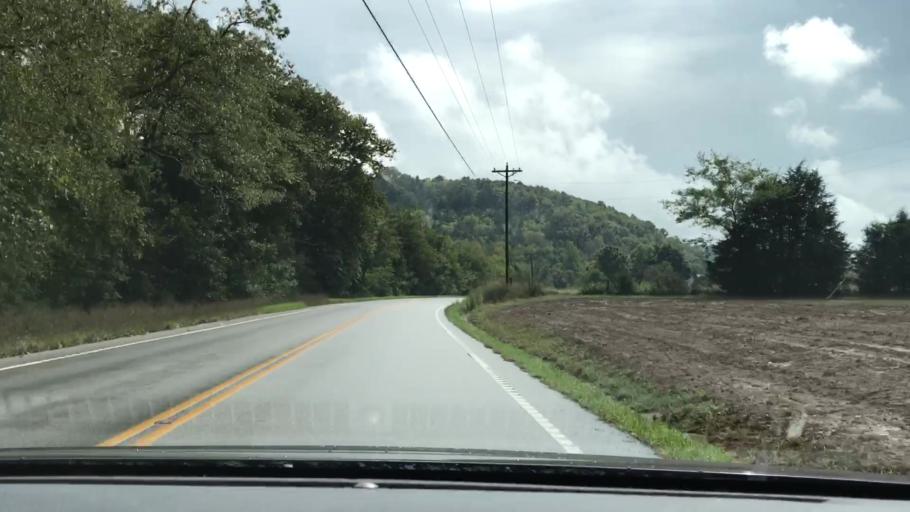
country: US
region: Tennessee
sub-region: Smith County
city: Carthage
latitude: 36.3416
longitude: -85.9655
